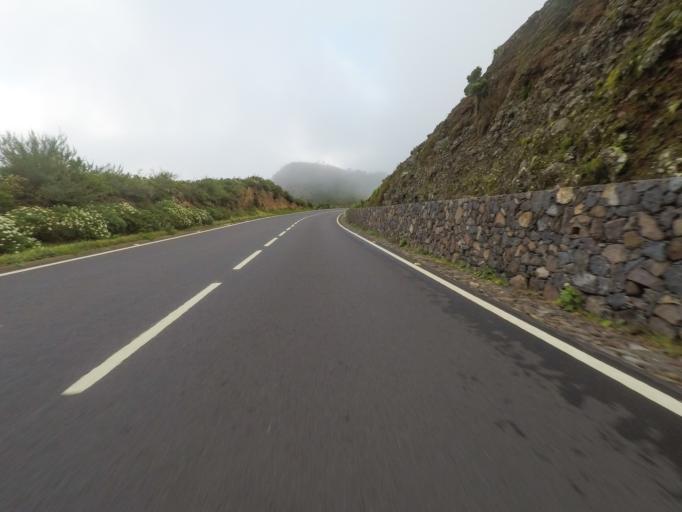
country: ES
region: Canary Islands
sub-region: Provincia de Santa Cruz de Tenerife
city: Alajero
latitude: 28.1060
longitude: -17.2120
